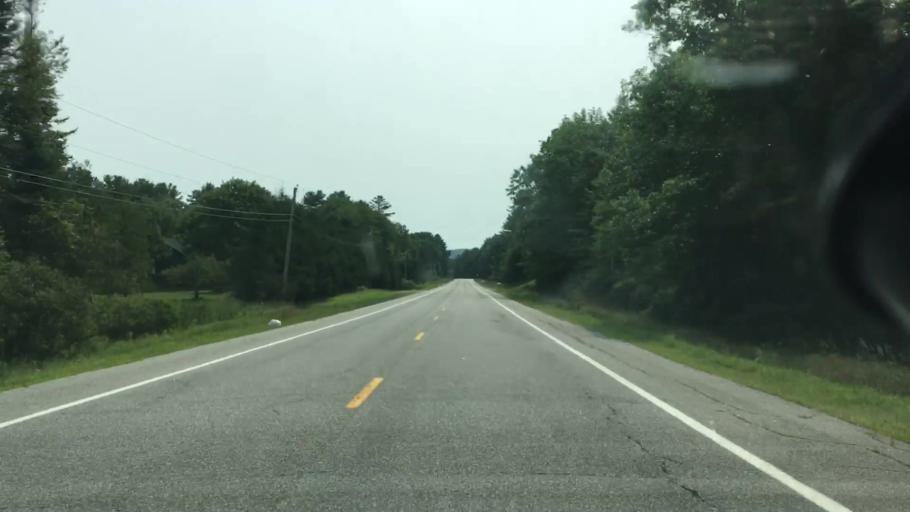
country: US
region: Maine
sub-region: Kennebec County
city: Wayne
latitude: 44.3665
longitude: -70.0897
